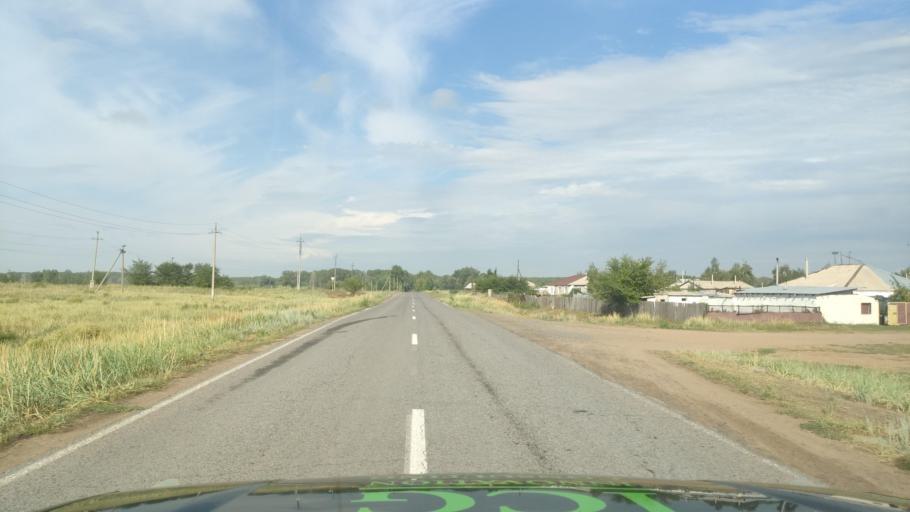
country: KZ
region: Pavlodar
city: Leninskiy
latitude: 52.4774
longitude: 76.8196
